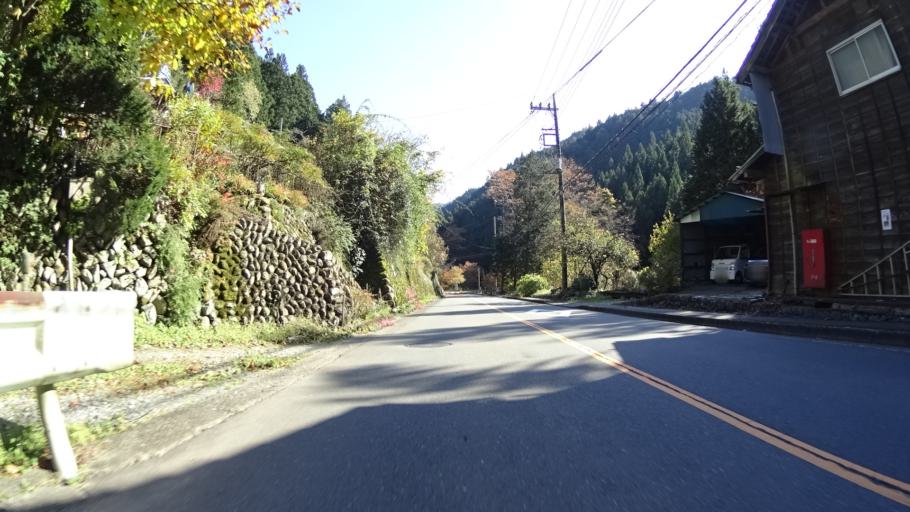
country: JP
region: Yamanashi
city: Uenohara
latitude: 35.7109
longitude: 139.0925
